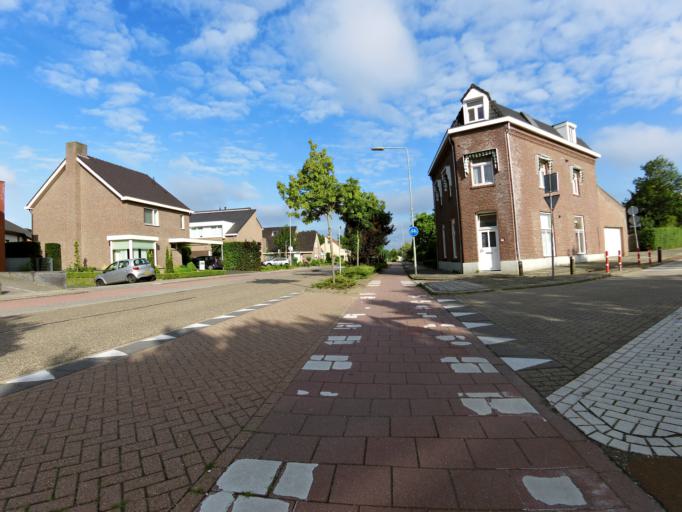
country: NL
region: Limburg
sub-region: Gemeente Heerlen
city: Heerlen
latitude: 50.8767
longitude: 6.0135
